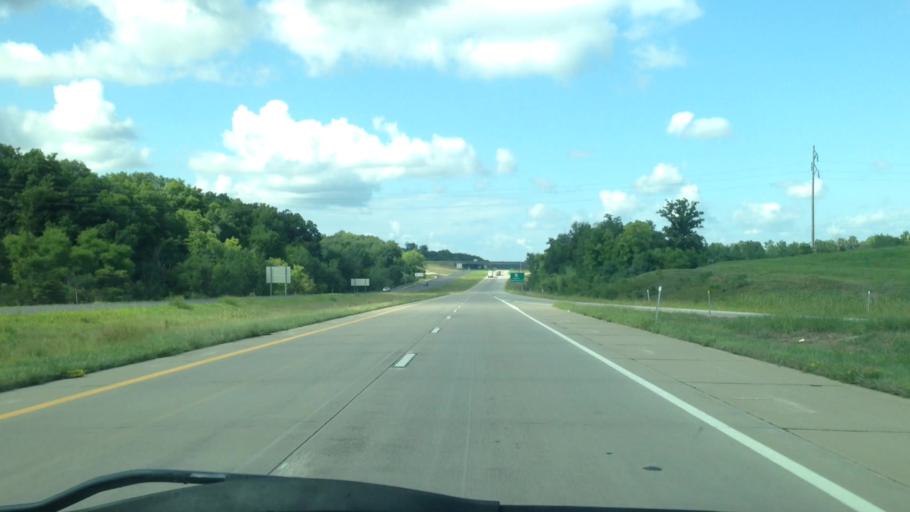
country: US
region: Missouri
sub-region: Lewis County
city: Canton
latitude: 40.1255
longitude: -91.5413
